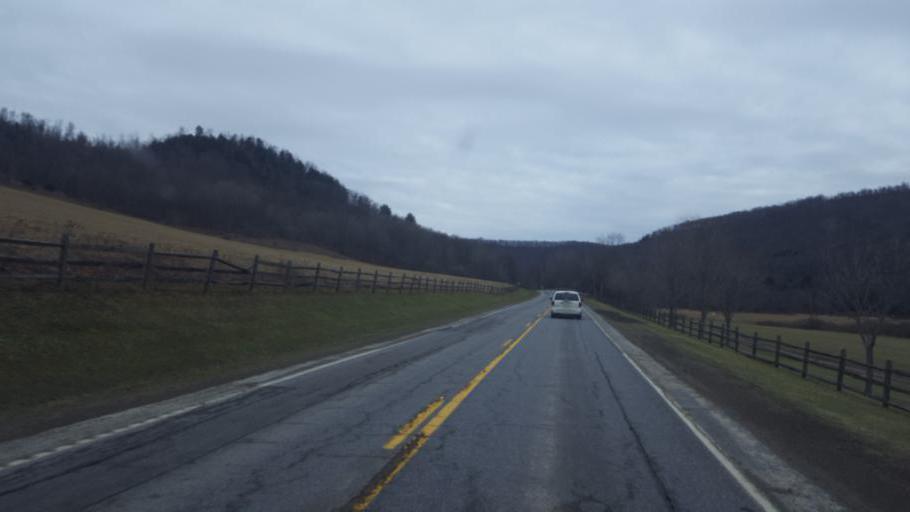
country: US
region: Pennsylvania
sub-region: Potter County
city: Coudersport
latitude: 41.8243
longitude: -77.9673
